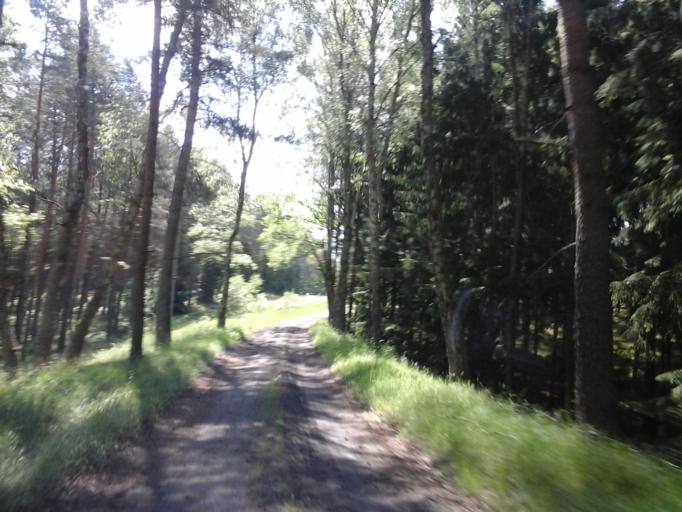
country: PL
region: West Pomeranian Voivodeship
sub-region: Powiat choszczenski
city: Bierzwnik
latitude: 53.0970
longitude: 15.7133
